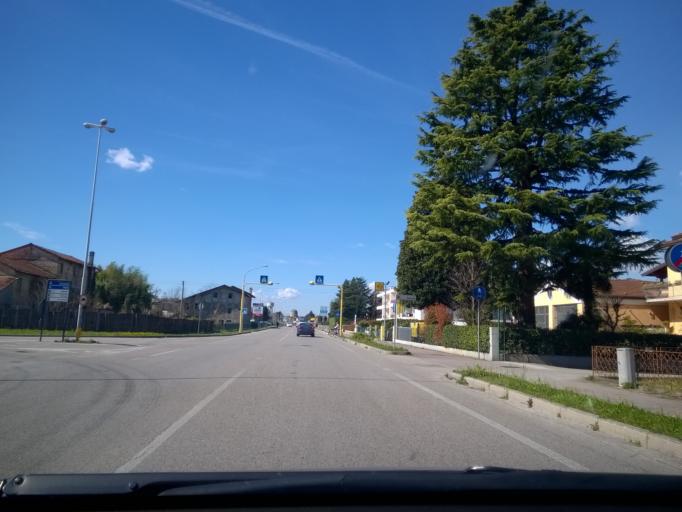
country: IT
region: Friuli Venezia Giulia
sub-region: Provincia di Pordenone
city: Sacile
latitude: 45.9621
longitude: 12.5186
